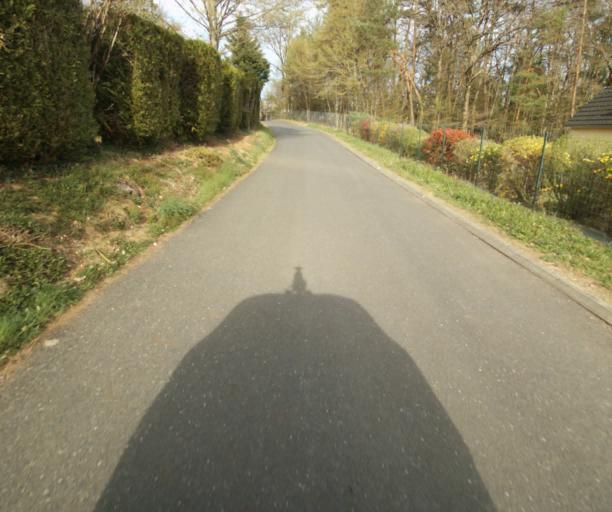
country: FR
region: Limousin
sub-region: Departement de la Correze
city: Naves
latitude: 45.3181
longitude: 1.7613
